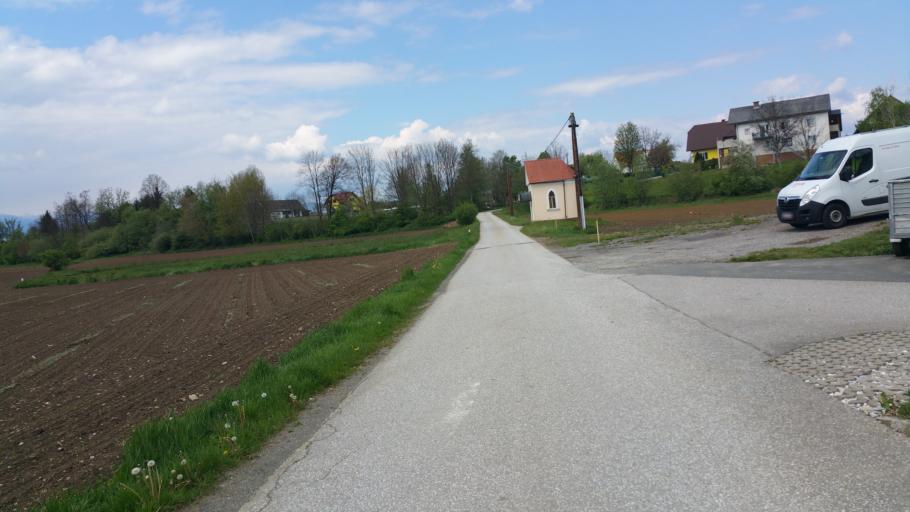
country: AT
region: Styria
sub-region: Politischer Bezirk Leibnitz
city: Gleinstatten
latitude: 46.7571
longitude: 15.3833
